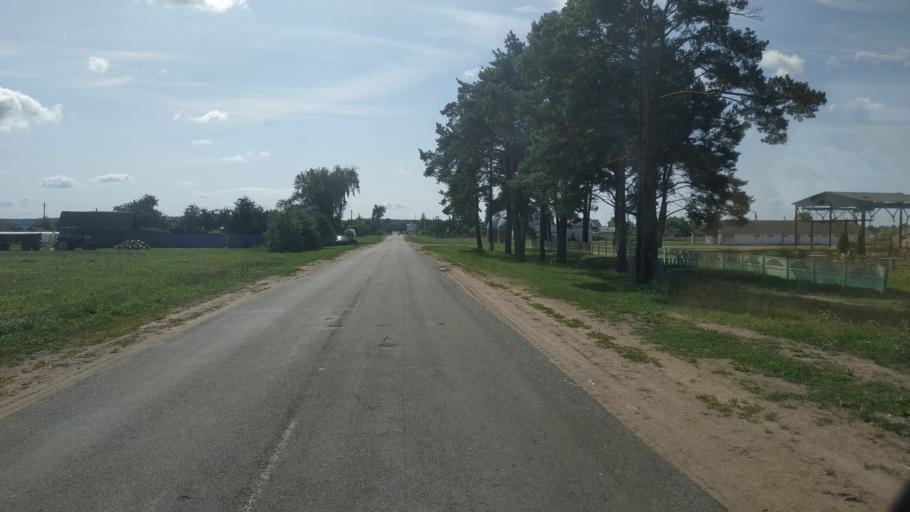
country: BY
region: Mogilev
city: Poselok Voskhod
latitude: 53.7099
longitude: 30.4986
